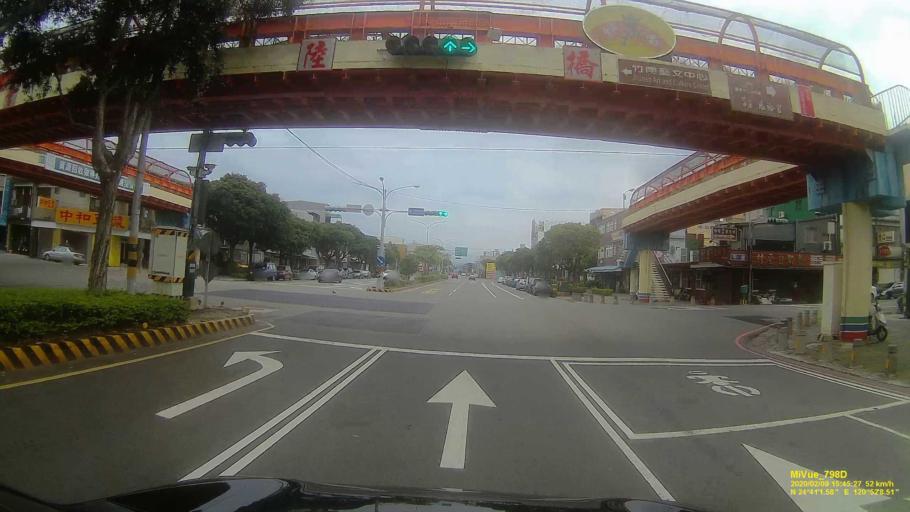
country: TW
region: Taiwan
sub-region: Miaoli
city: Miaoli
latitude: 24.6835
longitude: 120.8690
